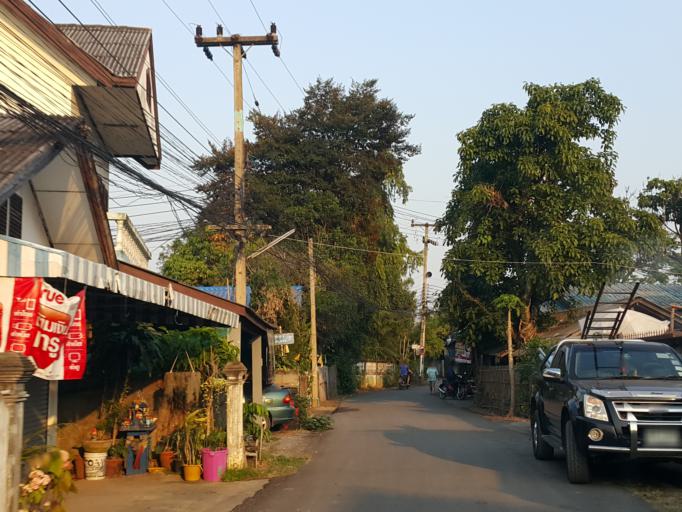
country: TH
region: Chiang Mai
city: San Sai
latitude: 18.9021
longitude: 98.9541
